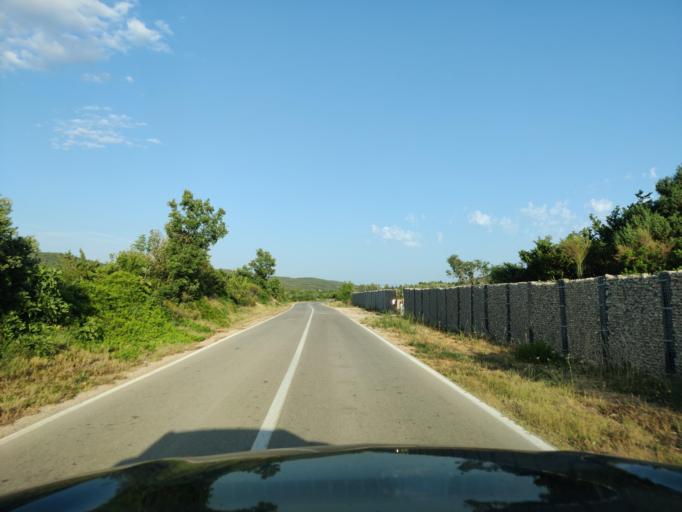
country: HR
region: Sibensko-Kniniska
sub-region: Grad Sibenik
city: Pirovac
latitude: 43.7894
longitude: 15.6968
